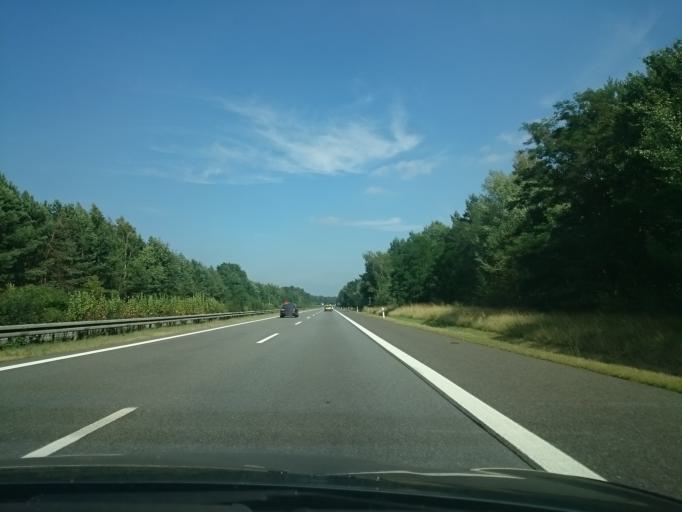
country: DE
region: Brandenburg
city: Calau
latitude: 51.7979
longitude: 13.8834
